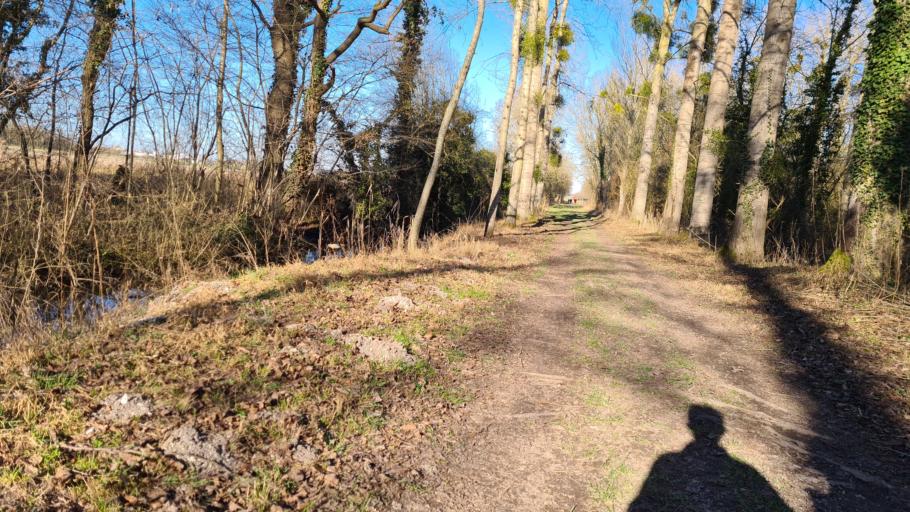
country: FR
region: Picardie
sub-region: Departement de l'Aisne
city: Bruyeres-et-Montberault
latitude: 49.5583
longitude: 3.6511
